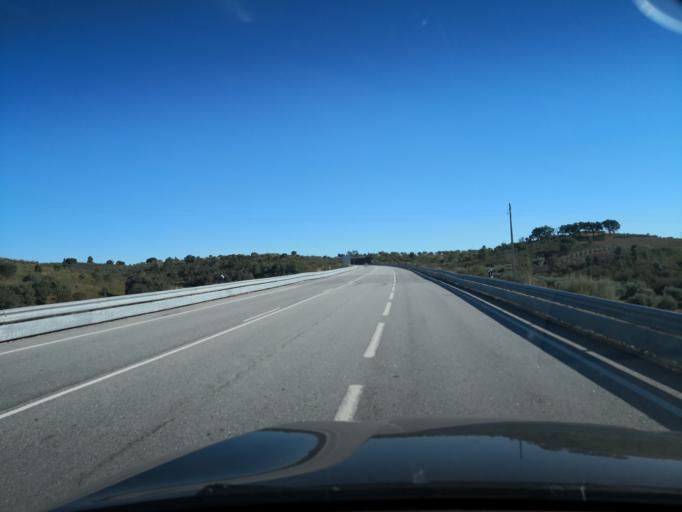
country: PT
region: Braganca
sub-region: Mirandela
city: Mirandela
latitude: 41.4964
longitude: -7.2290
